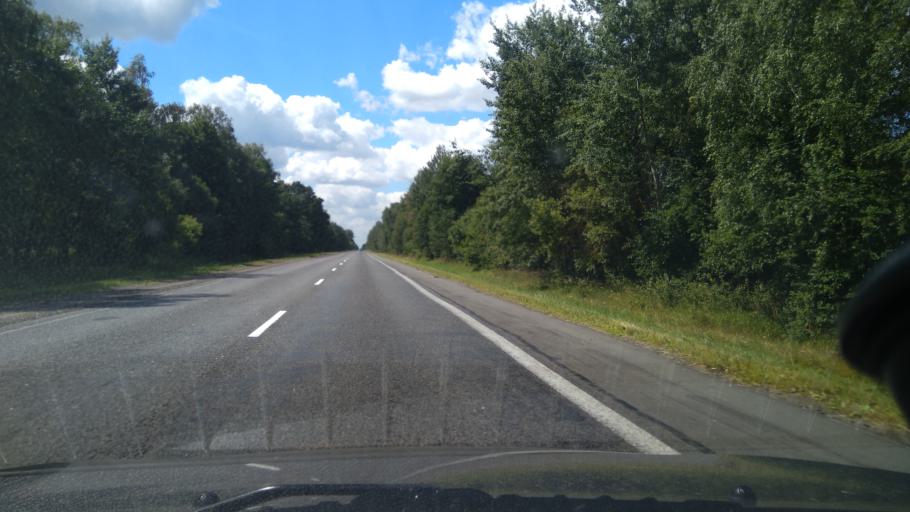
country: BY
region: Brest
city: Ivatsevichy
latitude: 52.6808
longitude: 25.2799
